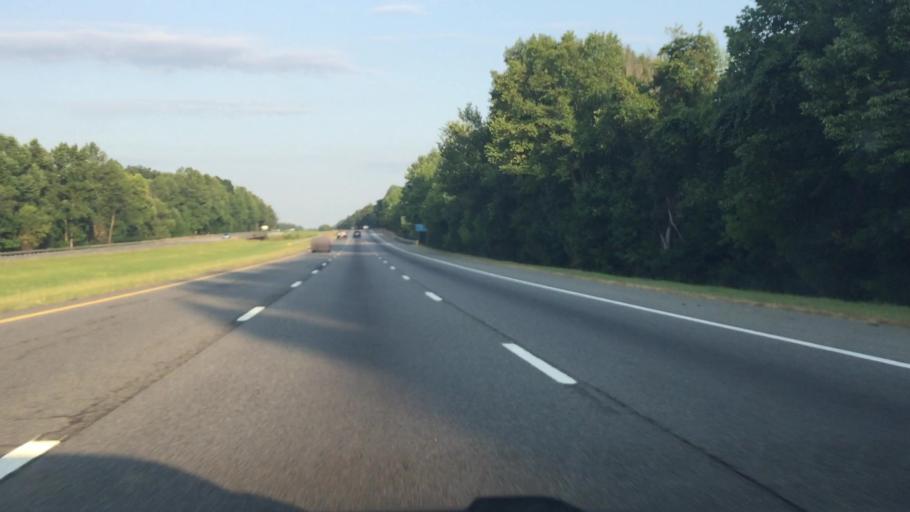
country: US
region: North Carolina
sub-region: Davidson County
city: Lexington
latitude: 35.7770
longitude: -80.2923
